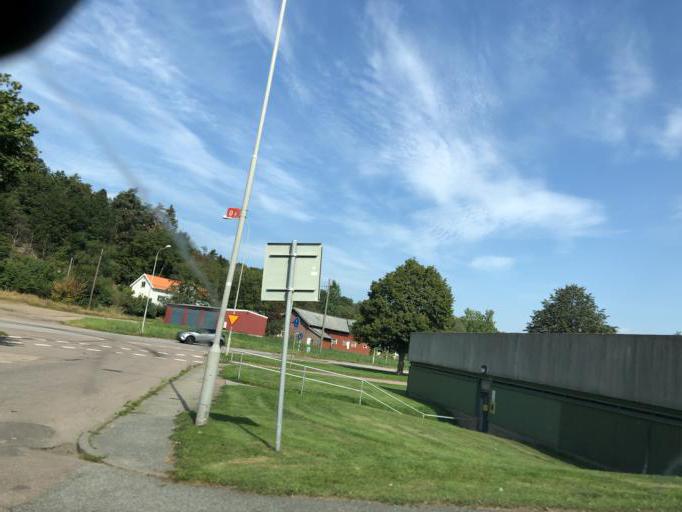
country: SE
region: Vaestra Goetaland
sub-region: Goteborg
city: Goeteborg
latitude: 57.7569
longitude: 11.9834
